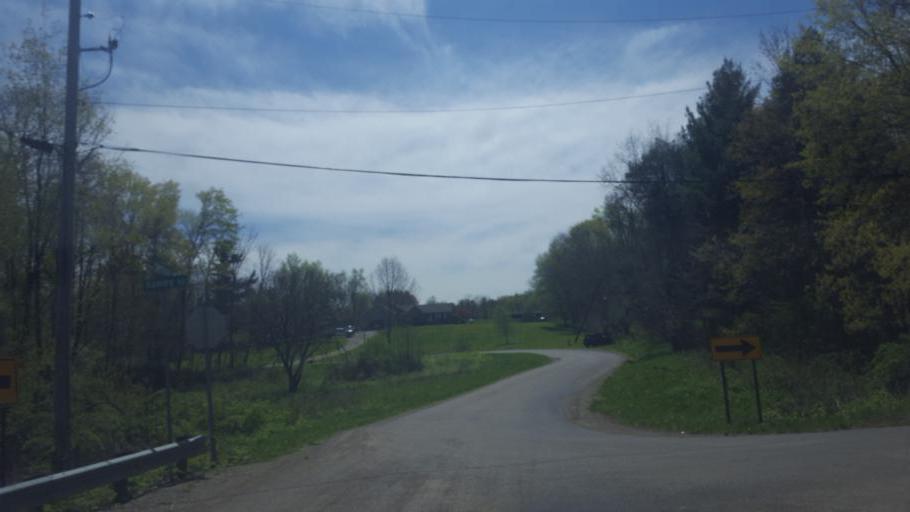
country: US
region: Ohio
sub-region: Richland County
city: Lincoln Heights
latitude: 40.6906
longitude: -82.4361
